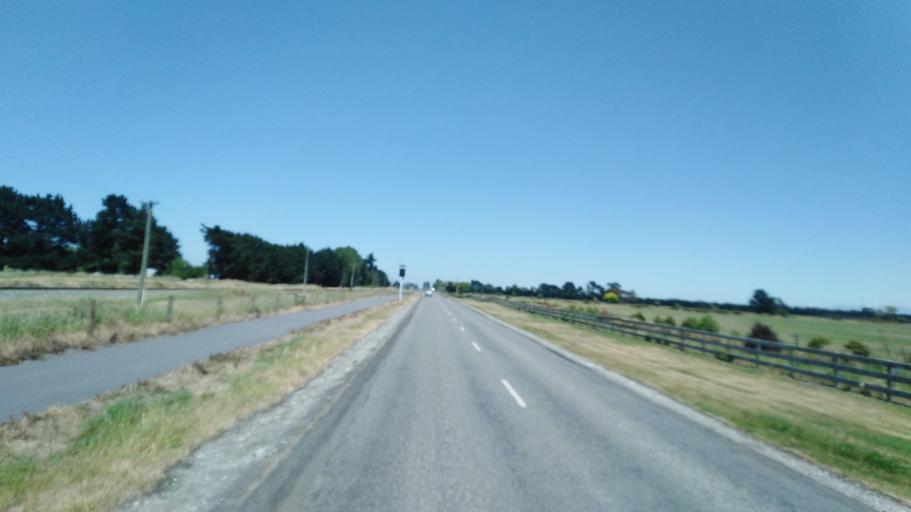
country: NZ
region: Canterbury
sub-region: Selwyn District
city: Prebbleton
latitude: -43.5626
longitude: 172.4516
